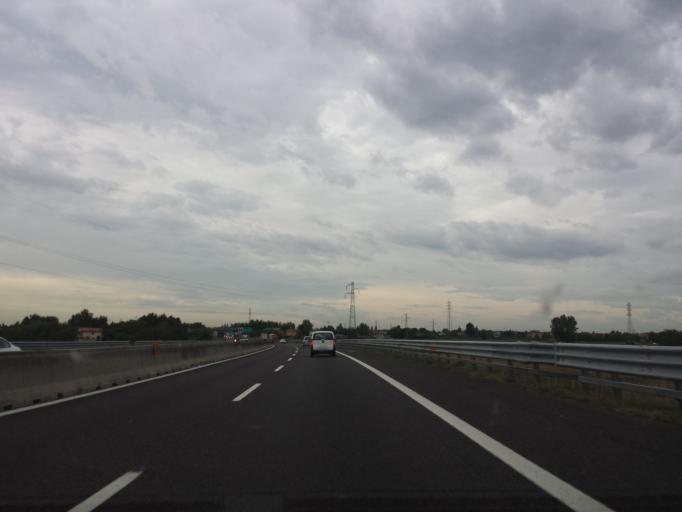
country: IT
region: Veneto
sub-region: Provincia di Padova
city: Pernumia
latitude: 45.2528
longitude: 11.7748
